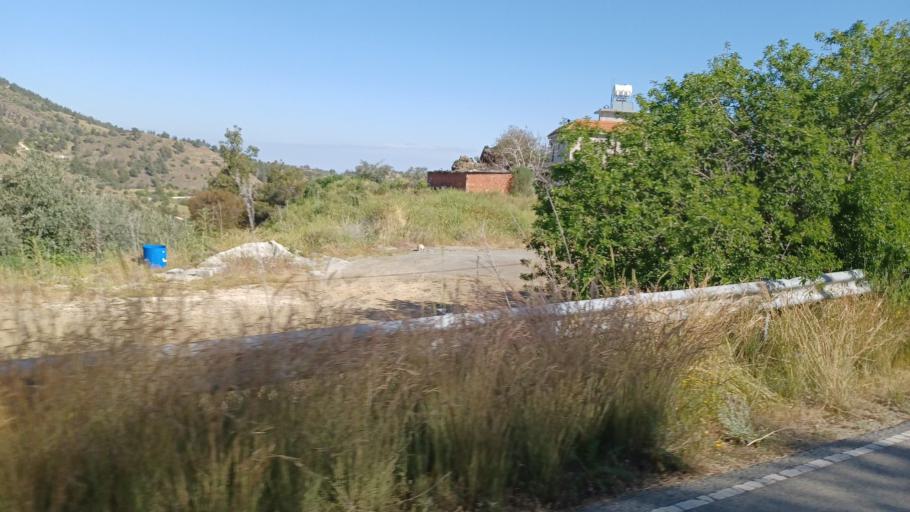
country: CY
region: Limassol
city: Kyperounta
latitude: 35.0271
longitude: 33.0380
